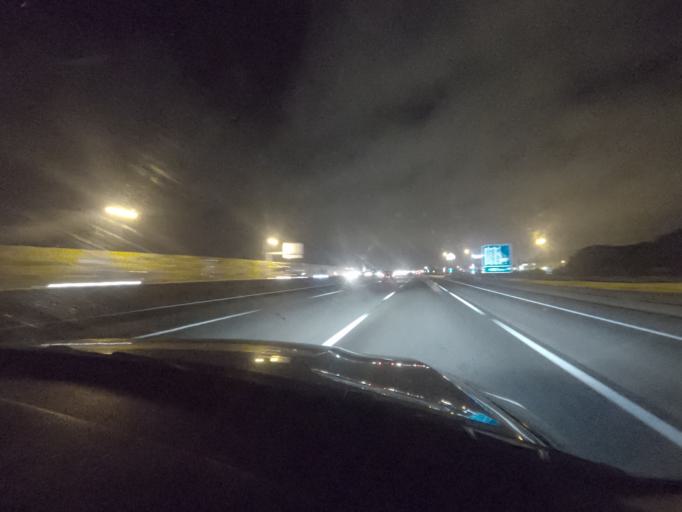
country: PT
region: Lisbon
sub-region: Vila Franca de Xira
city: Castanheira do Ribatejo
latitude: 39.0048
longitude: -8.9671
